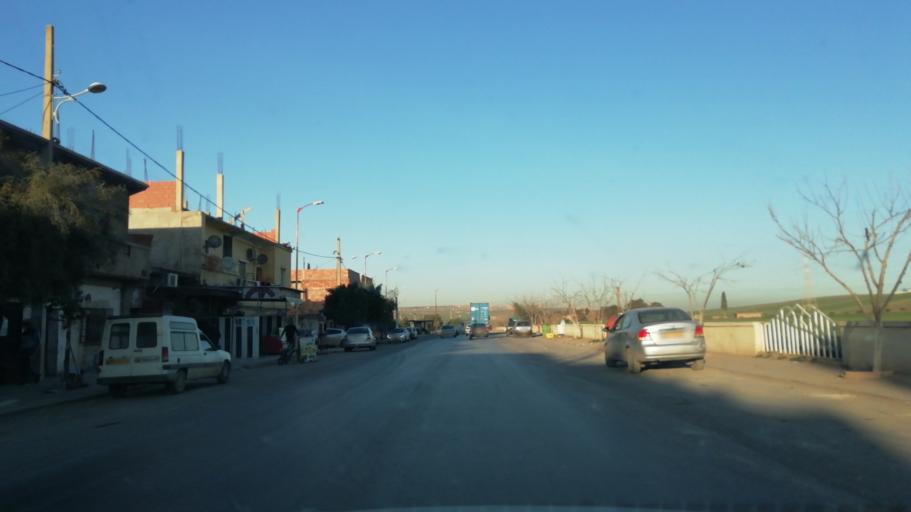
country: DZ
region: Oran
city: Es Senia
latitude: 35.5625
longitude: -0.5639
